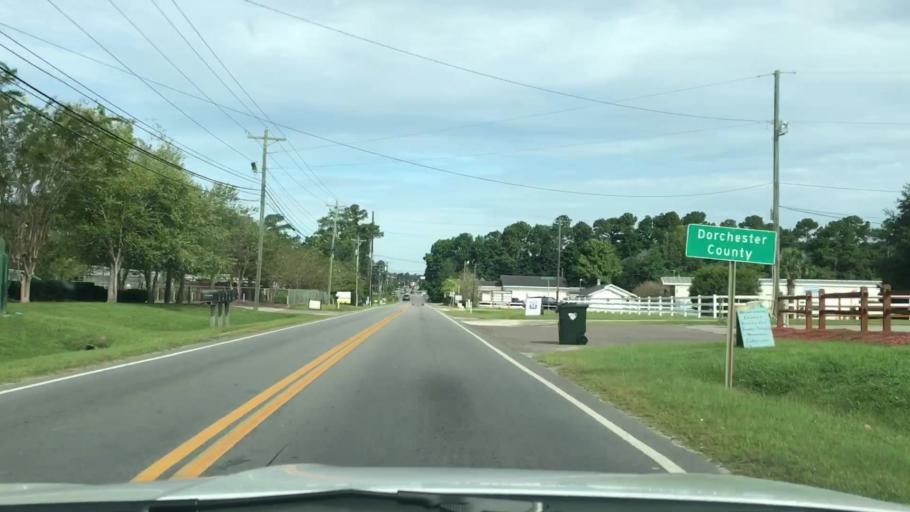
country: US
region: South Carolina
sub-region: Dorchester County
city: Summerville
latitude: 33.0210
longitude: -80.1608
